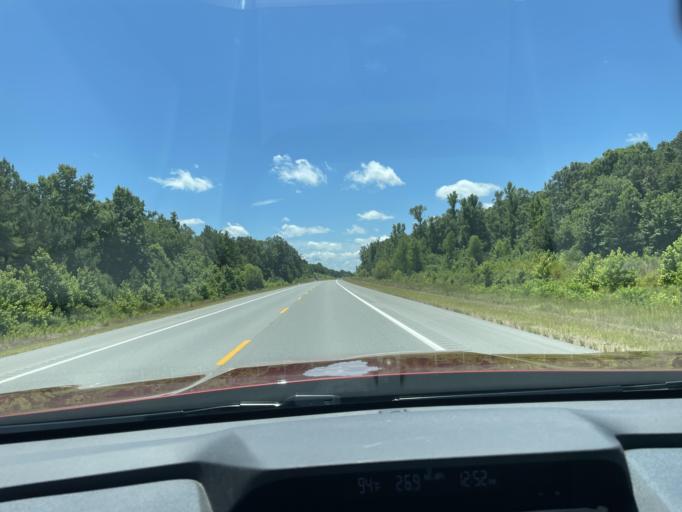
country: US
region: Arkansas
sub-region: Lincoln County
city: Star City
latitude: 33.9162
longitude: -91.8840
